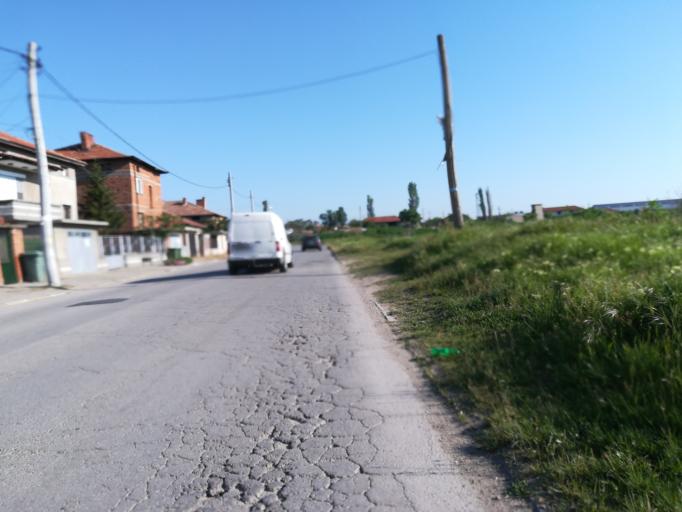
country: BG
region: Stara Zagora
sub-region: Obshtina Chirpan
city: Chirpan
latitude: 42.1063
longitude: 25.2273
